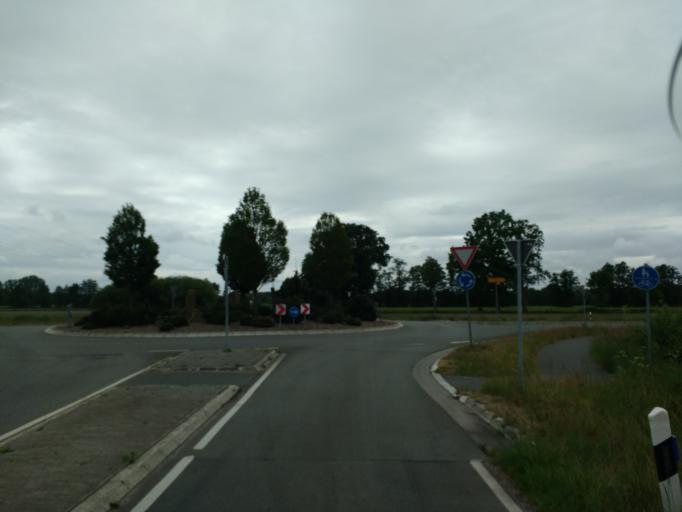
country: DE
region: Lower Saxony
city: Steinfeld
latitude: 52.6245
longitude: 8.1736
